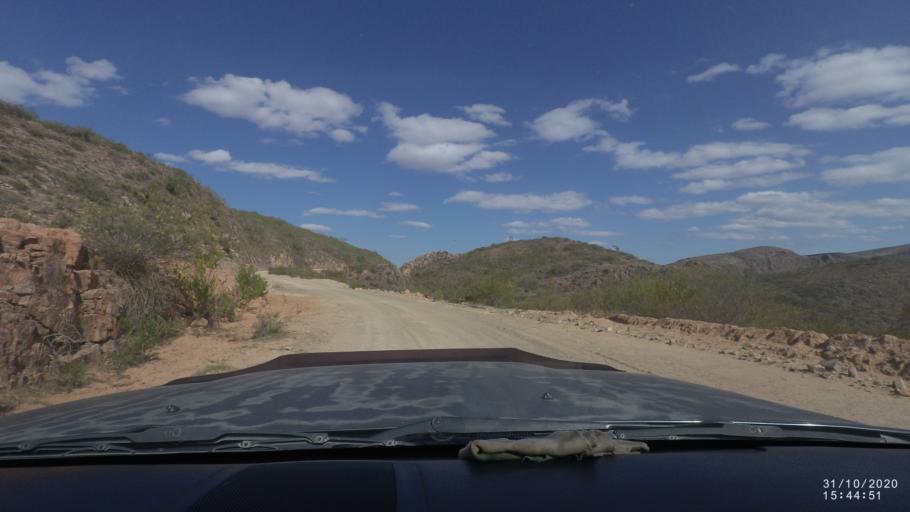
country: BO
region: Chuquisaca
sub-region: Provincia Zudanez
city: Mojocoya
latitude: -18.3180
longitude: -64.7211
